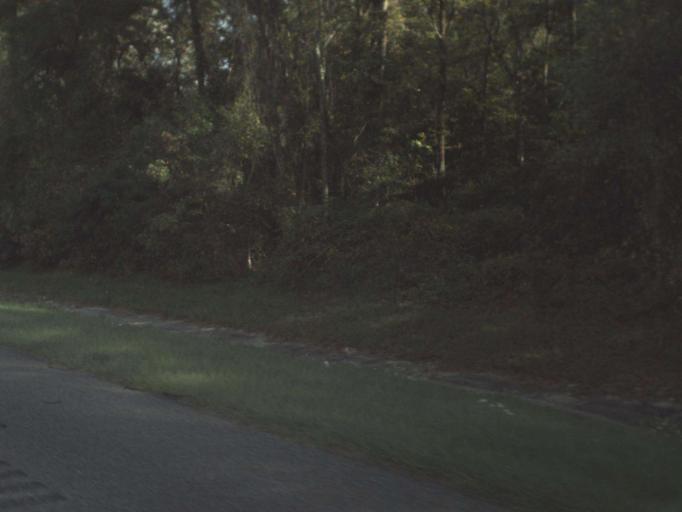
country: US
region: Florida
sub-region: Jefferson County
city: Monticello
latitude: 30.4731
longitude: -83.8648
